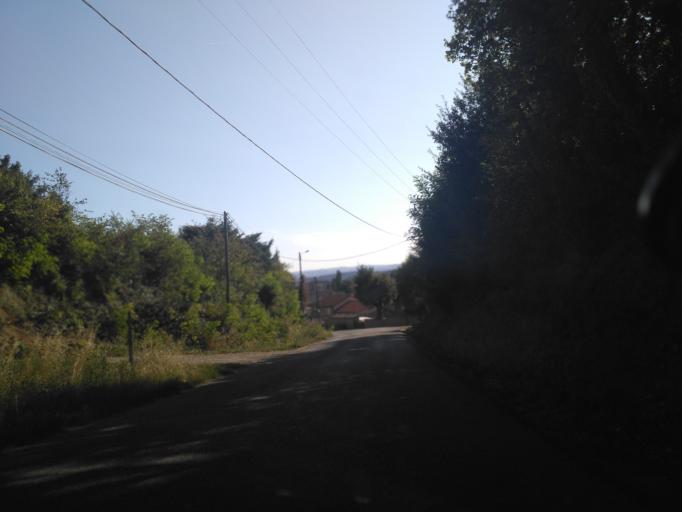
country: FR
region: Rhone-Alpes
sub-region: Departement de la Drome
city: Clerieux
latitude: 45.1272
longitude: 4.9873
